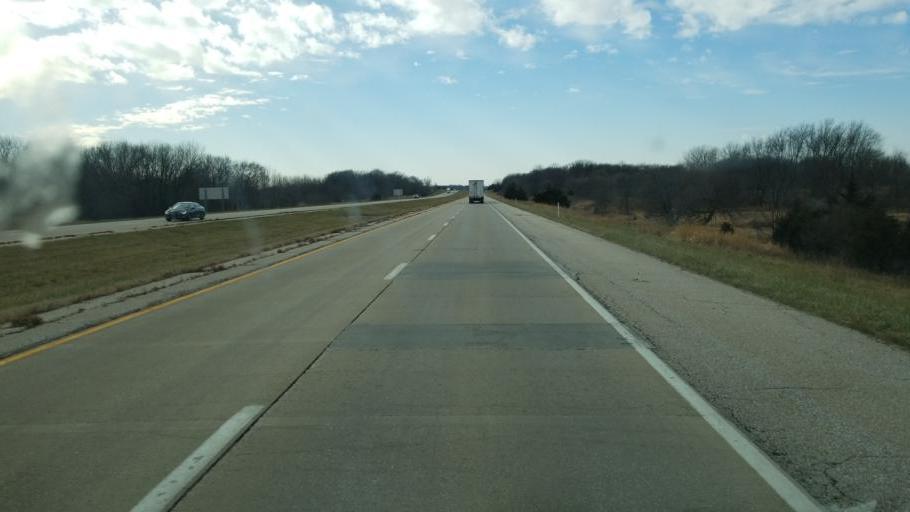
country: US
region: Illinois
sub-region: Knox County
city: Galesburg
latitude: 40.9315
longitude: -90.4238
